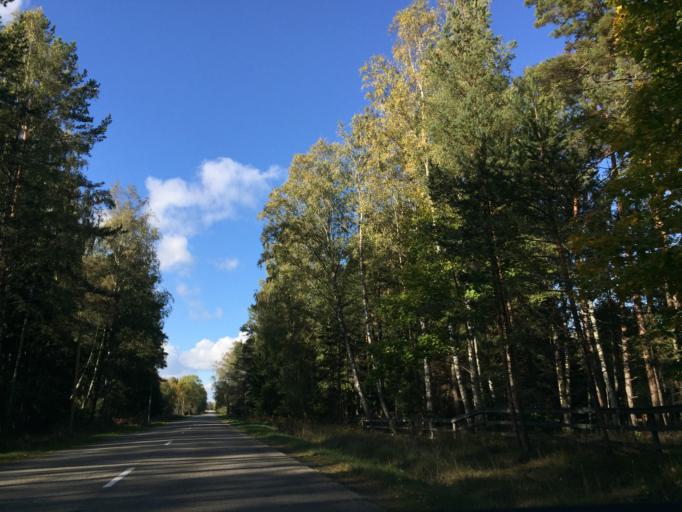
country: LV
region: Rojas
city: Roja
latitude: 57.4173
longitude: 22.9350
